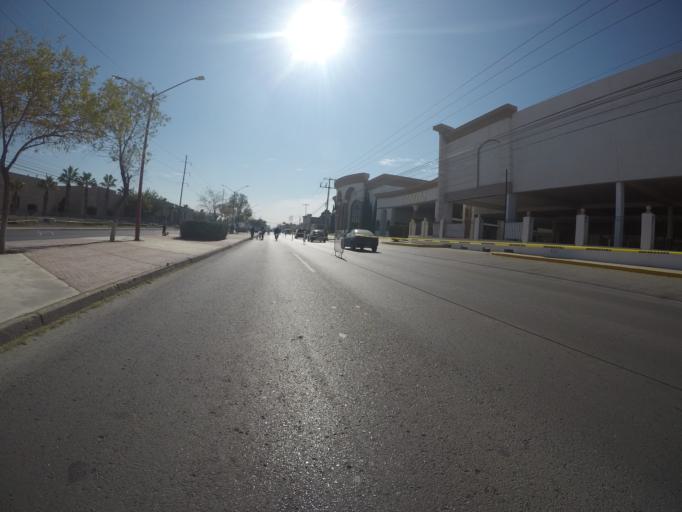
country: MX
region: Chihuahua
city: Ciudad Juarez
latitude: 31.7220
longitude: -106.3994
